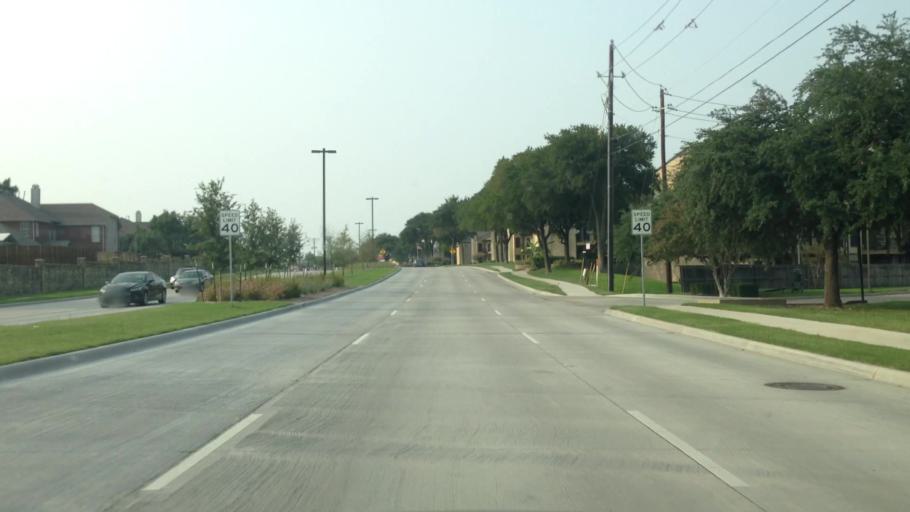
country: US
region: Texas
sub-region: Dallas County
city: Carrollton
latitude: 33.0079
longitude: -96.9100
